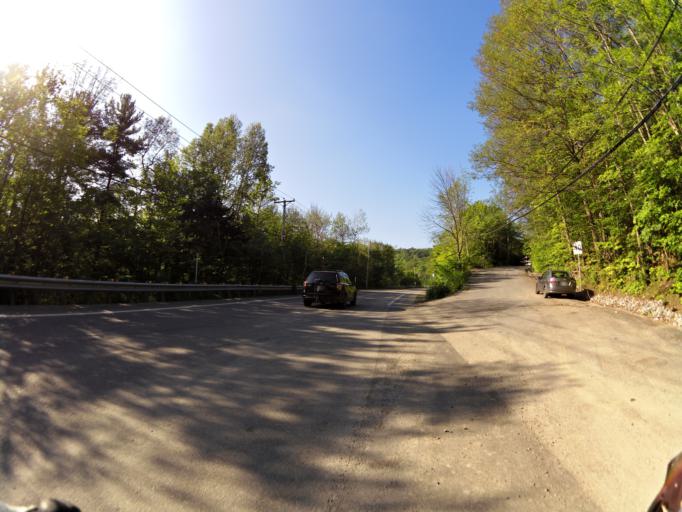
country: CA
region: Quebec
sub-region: Outaouais
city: Wakefield
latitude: 45.5475
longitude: -75.8211
